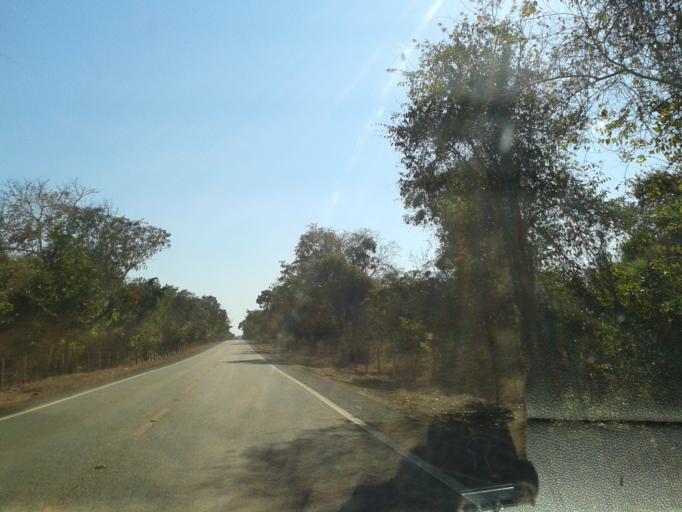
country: BR
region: Goias
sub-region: Mozarlandia
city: Mozarlandia
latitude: -14.6733
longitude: -50.5354
